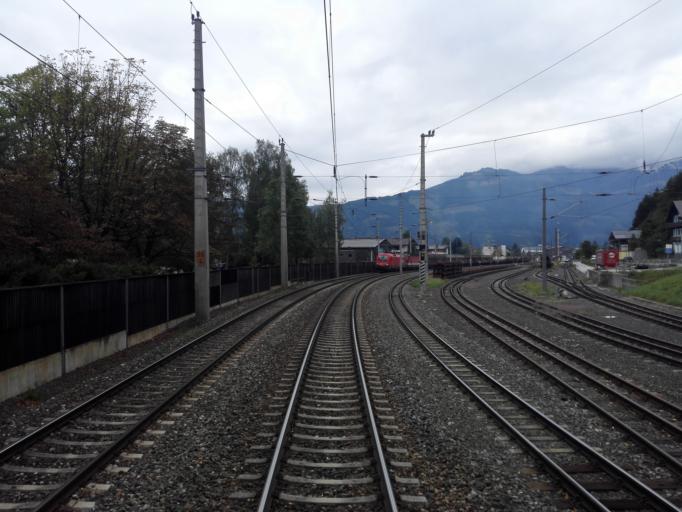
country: AT
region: Salzburg
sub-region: Politischer Bezirk Zell am See
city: Zell am See
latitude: 47.3125
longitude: 12.7946
